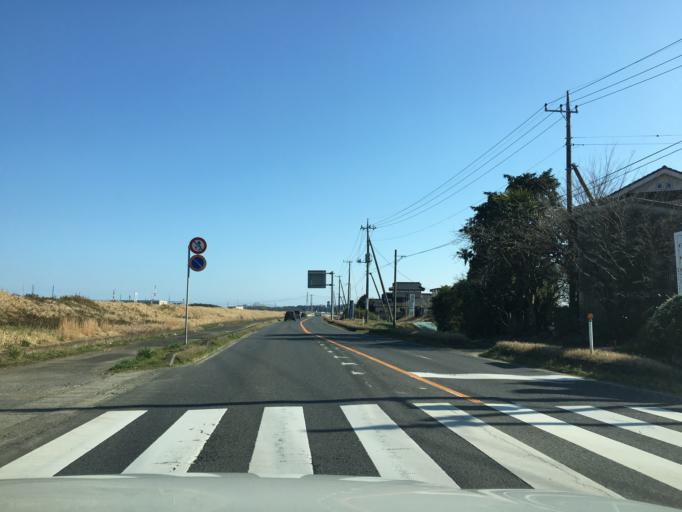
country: JP
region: Ibaraki
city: Mito-shi
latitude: 36.4369
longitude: 140.4176
